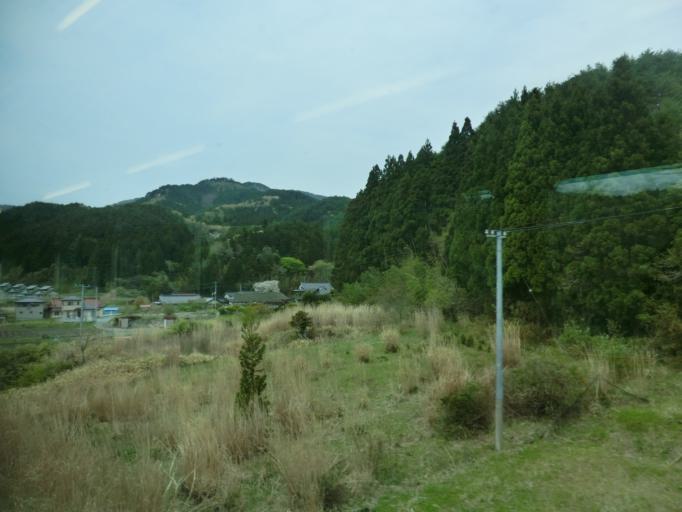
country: JP
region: Iwate
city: Ofunato
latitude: 39.0543
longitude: 141.7909
